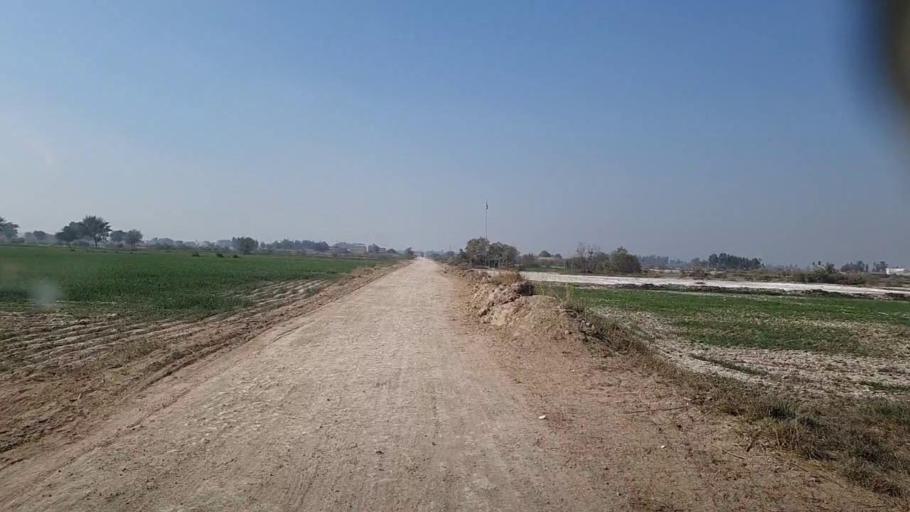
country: PK
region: Sindh
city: Khairpur
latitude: 27.9936
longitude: 69.6966
